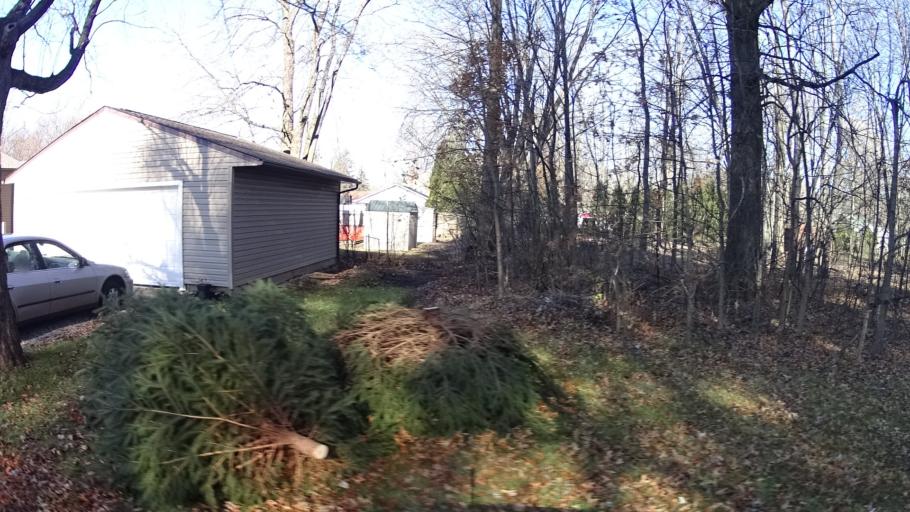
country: US
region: Ohio
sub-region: Lorain County
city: North Ridgeville
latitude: 41.4116
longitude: -81.9889
